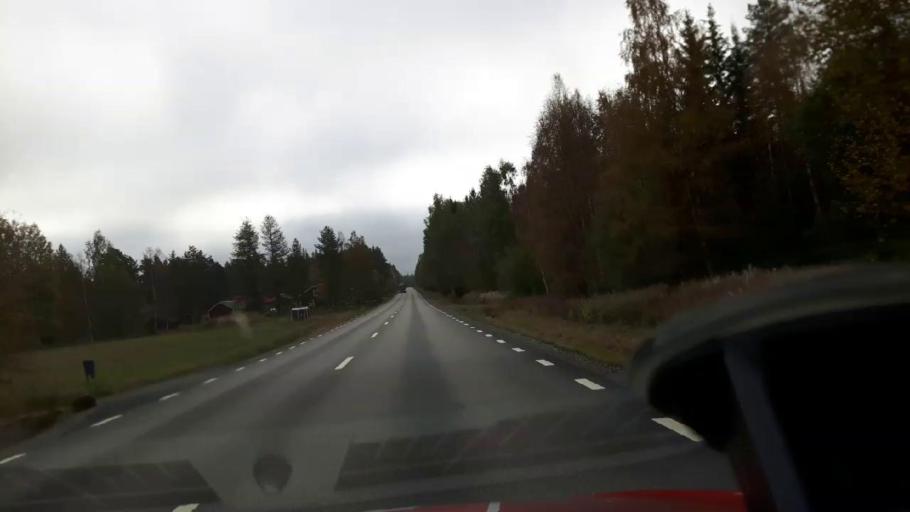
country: SE
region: Gaevleborg
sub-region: Ljusdals Kommun
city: Farila
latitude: 61.8590
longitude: 15.7434
